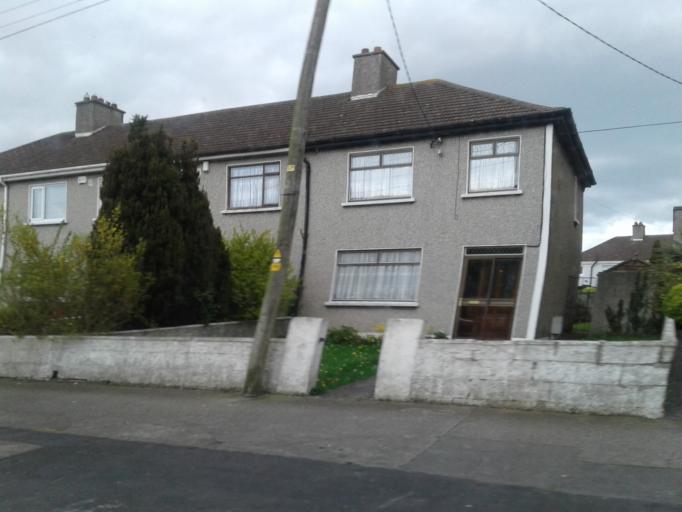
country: IE
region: Leinster
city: Artane
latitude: 53.3857
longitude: -6.2160
